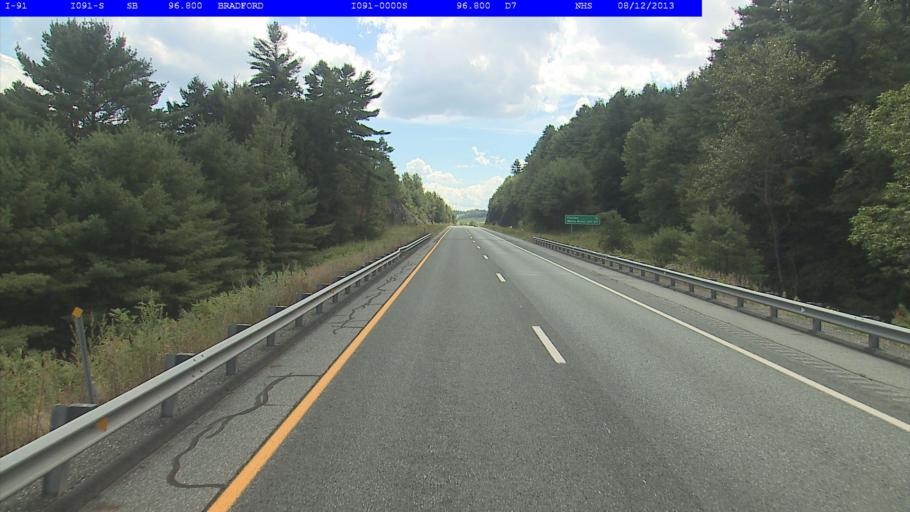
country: US
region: New Hampshire
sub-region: Grafton County
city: Orford
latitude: 43.9730
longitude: -72.1262
